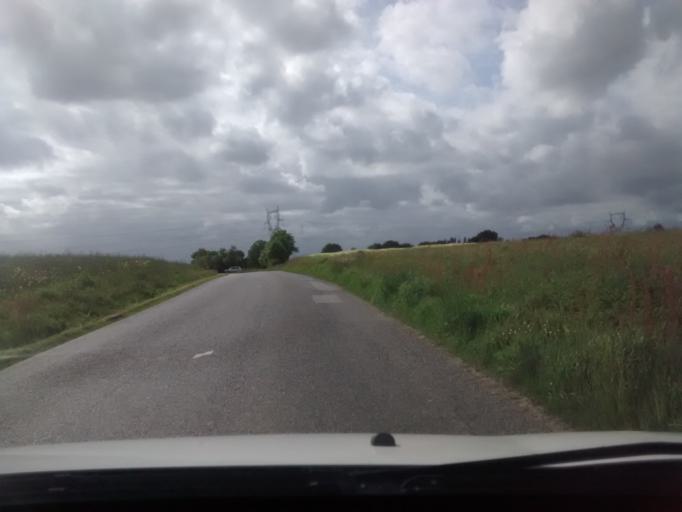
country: FR
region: Brittany
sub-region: Departement d'Ille-et-Vilaine
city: Nouvoitou
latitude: 48.0692
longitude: -1.5325
